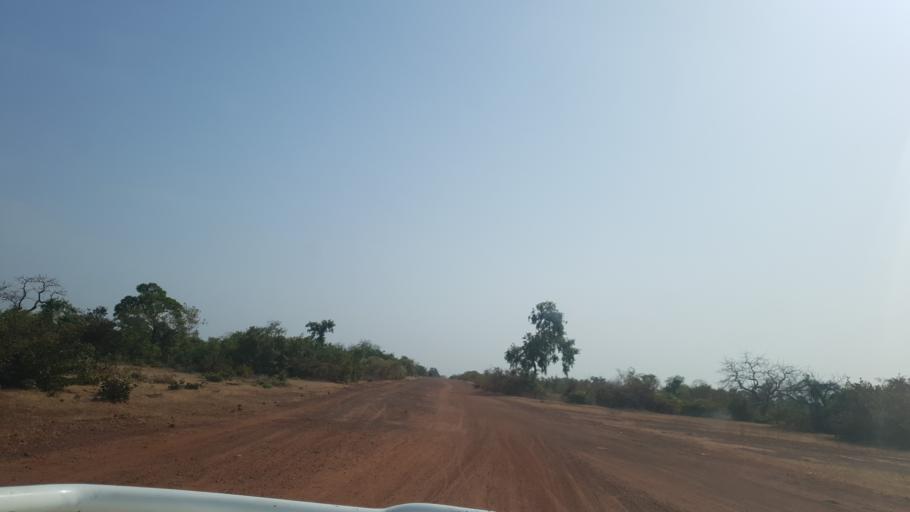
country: ML
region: Koulikoro
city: Dioila
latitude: 12.6676
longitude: -6.6962
